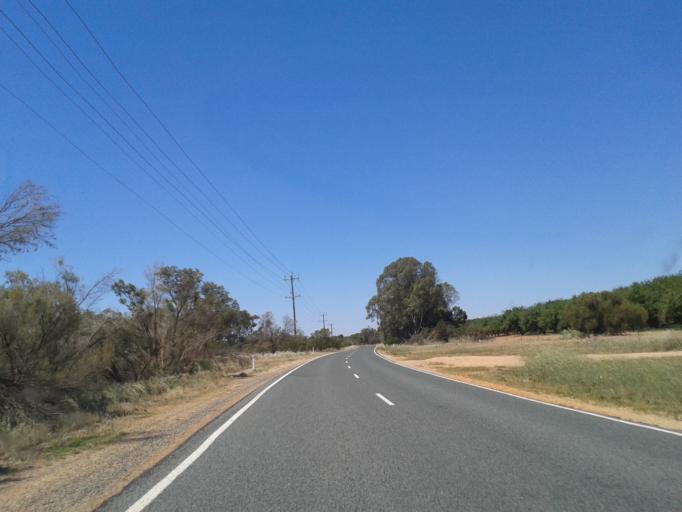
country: AU
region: Victoria
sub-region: Mildura Shire
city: Ouyen
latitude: -34.7118
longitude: 142.9276
